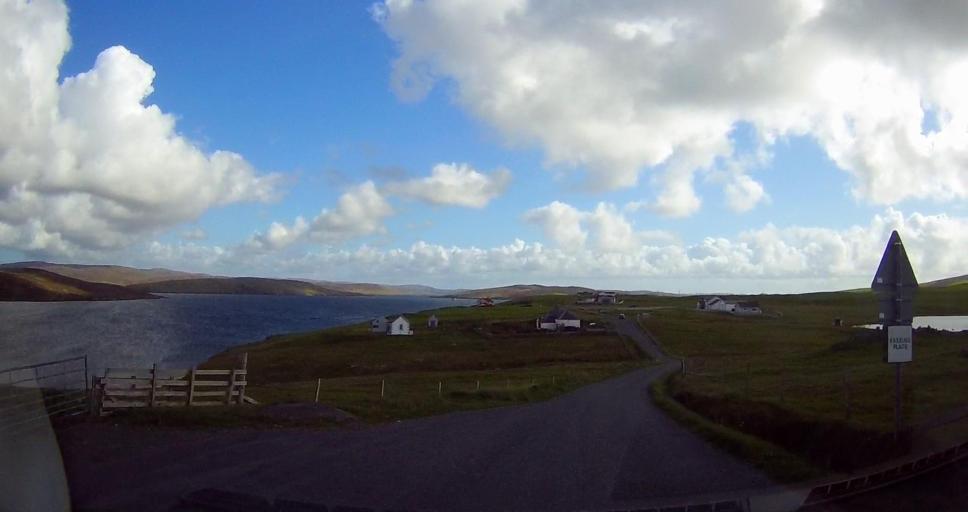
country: GB
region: Scotland
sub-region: Shetland Islands
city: Lerwick
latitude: 60.3670
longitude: -1.3818
